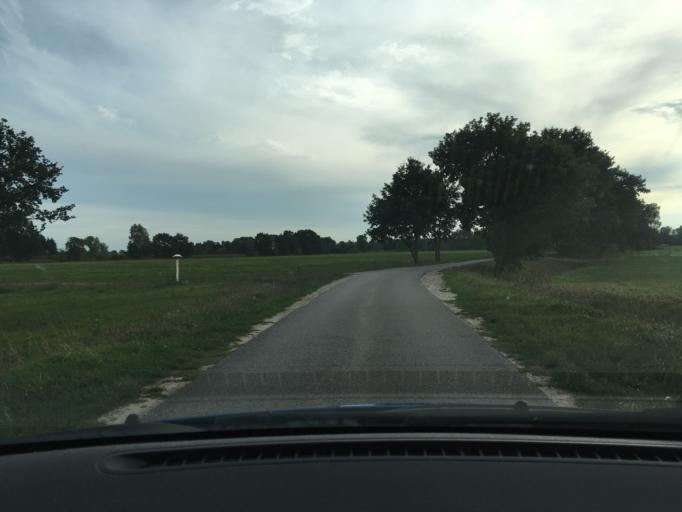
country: DE
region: Lower Saxony
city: Wietzendorf
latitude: 52.8947
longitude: 9.9524
